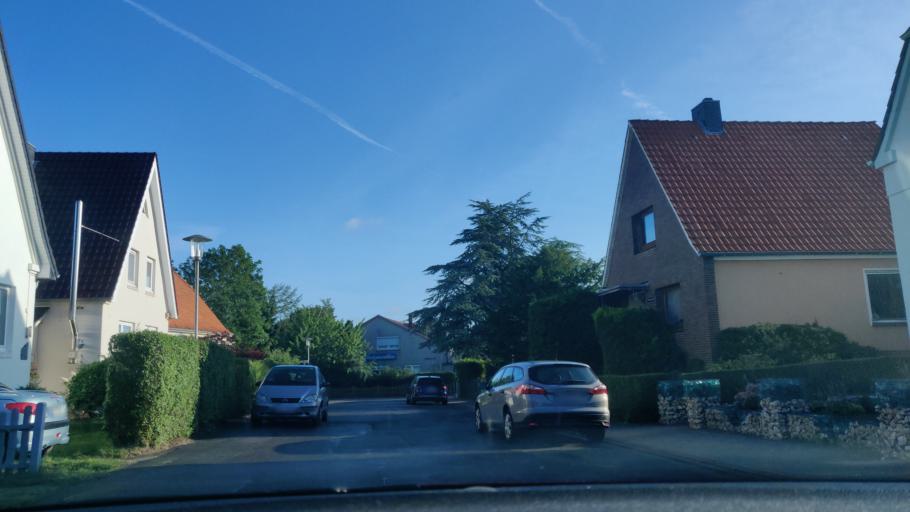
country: DE
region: Lower Saxony
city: Cuxhaven
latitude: 53.8851
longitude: 8.6684
